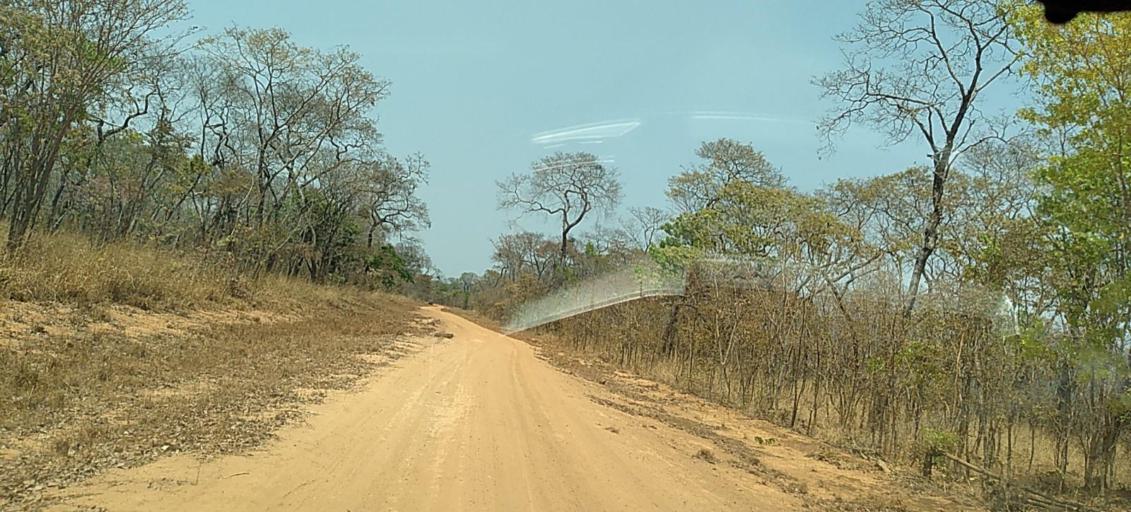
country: ZM
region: Central
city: Mumbwa
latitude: -14.3803
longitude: 26.4813
